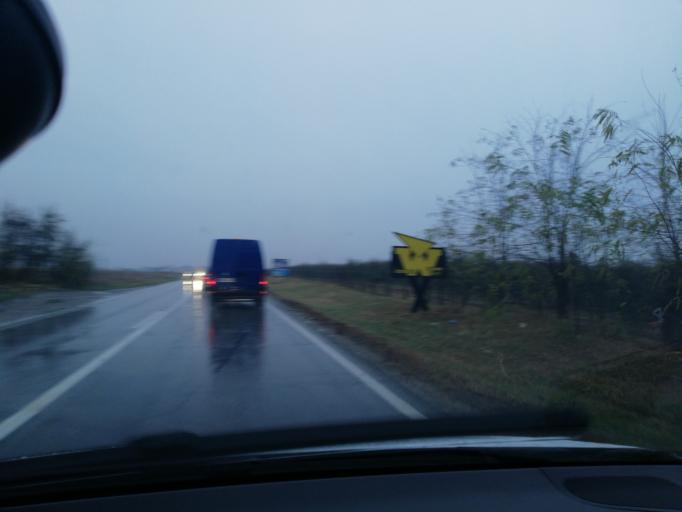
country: RS
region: Autonomna Pokrajina Vojvodina
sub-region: Sremski Okrug
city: Ruma
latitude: 45.0305
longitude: 19.8354
